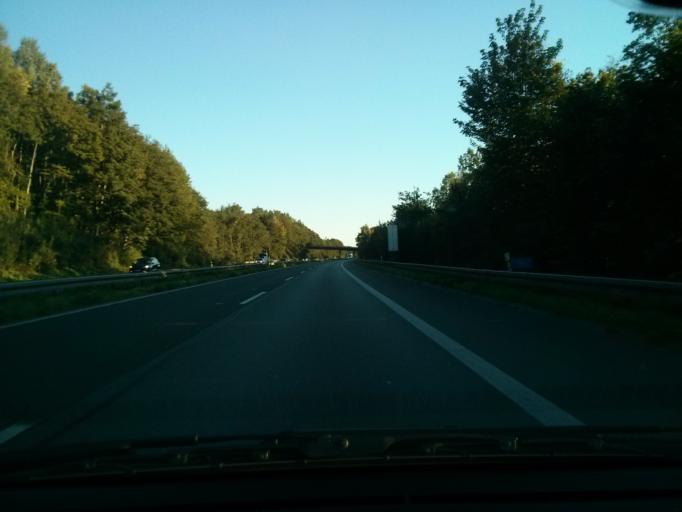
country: DE
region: North Rhine-Westphalia
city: Wickede
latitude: 51.4945
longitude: 7.9241
